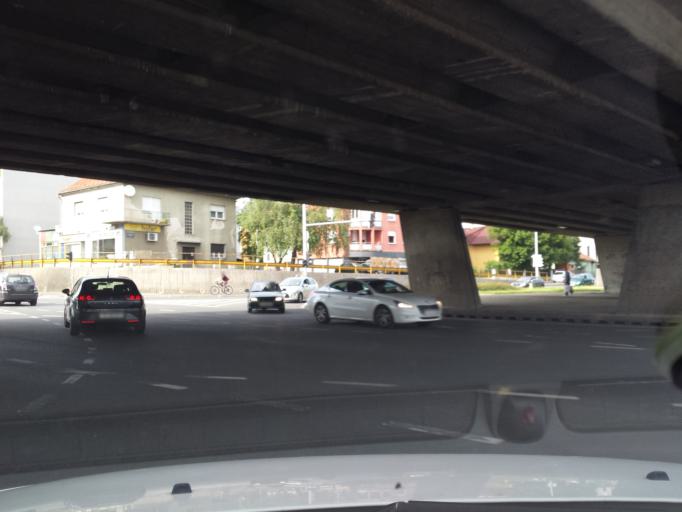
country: HR
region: Grad Zagreb
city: Zagreb - Centar
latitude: 45.7940
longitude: 15.9441
